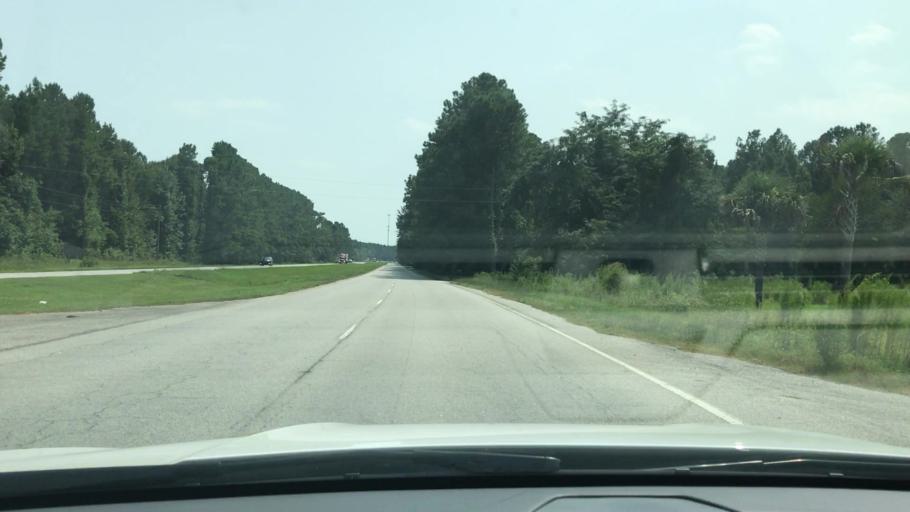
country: US
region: South Carolina
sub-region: Charleston County
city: Awendaw
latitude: 33.0014
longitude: -79.6438
